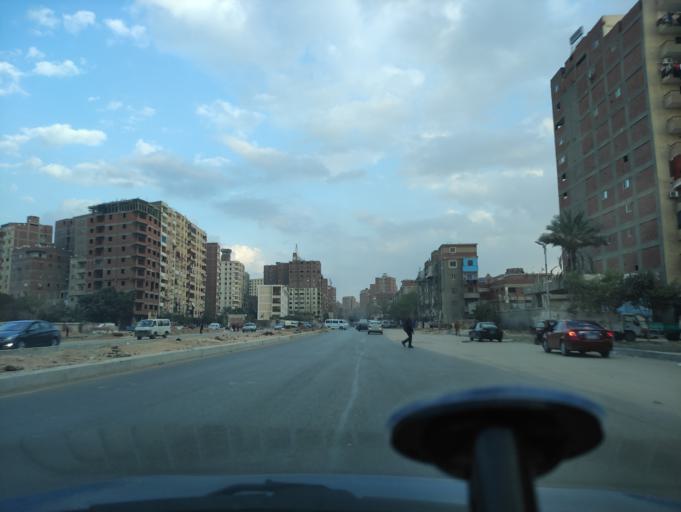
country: EG
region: Muhafazat al Qalyubiyah
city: Al Khankah
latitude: 30.1345
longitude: 31.3556
